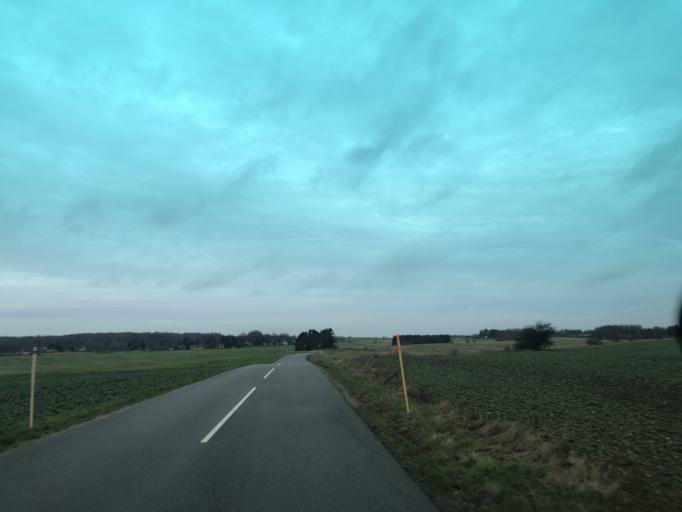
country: DK
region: Capital Region
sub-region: Allerod Kommune
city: Lynge
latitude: 55.8575
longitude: 12.2342
